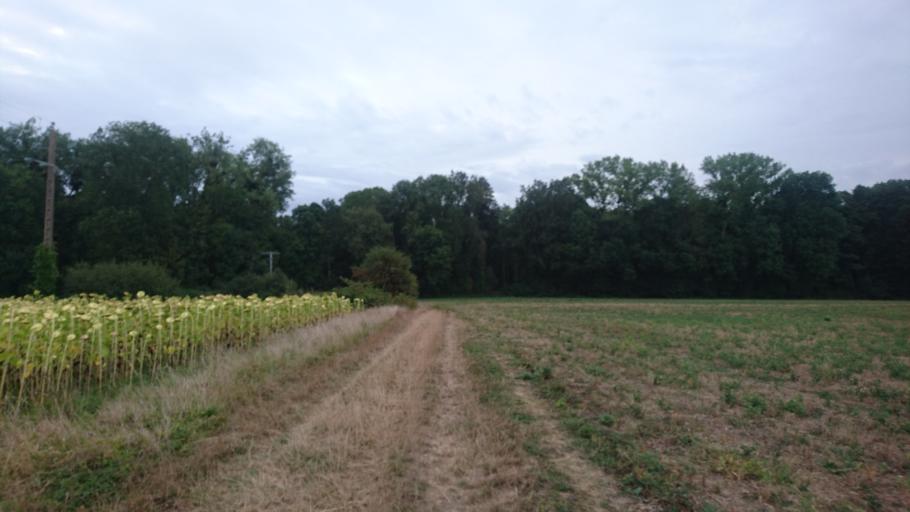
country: FR
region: Bourgogne
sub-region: Departement de l'Yonne
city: Aillant-sur-Tholon
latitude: 47.8658
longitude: 3.3983
